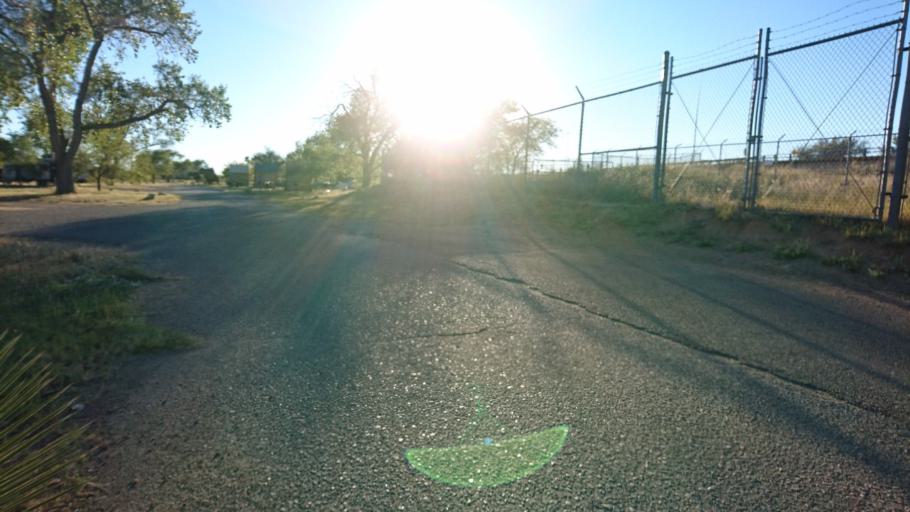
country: US
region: New Mexico
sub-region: Quay County
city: Tucumcari
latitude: 35.1713
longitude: -103.6679
